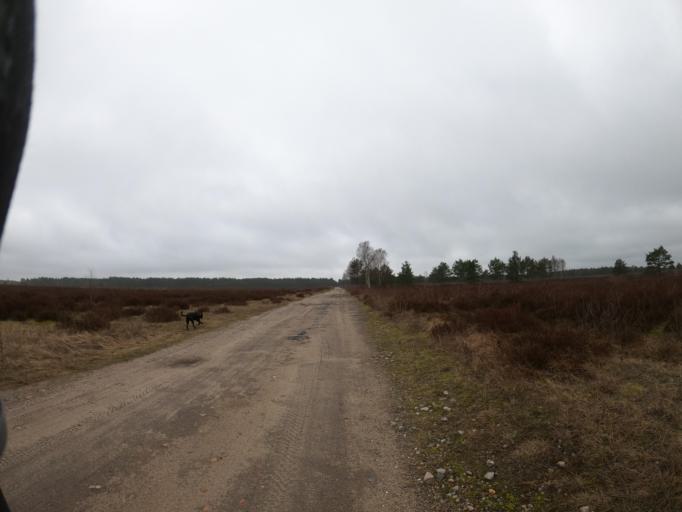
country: PL
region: West Pomeranian Voivodeship
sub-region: Powiat szczecinecki
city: Borne Sulinowo
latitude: 53.5202
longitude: 16.5638
